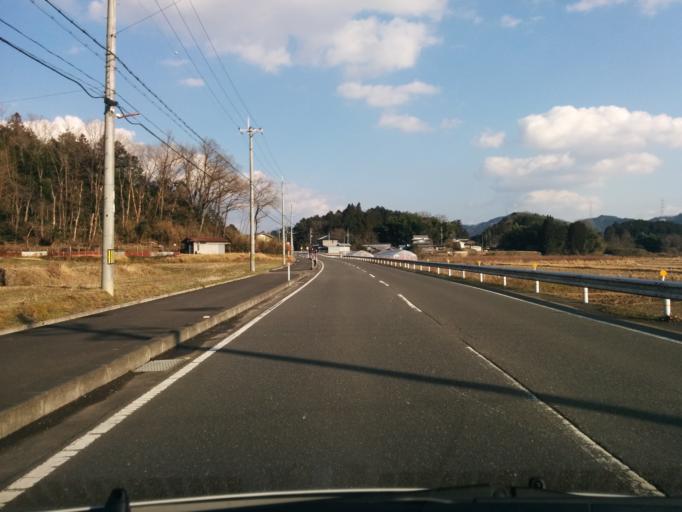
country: JP
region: Kyoto
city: Ayabe
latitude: 35.3613
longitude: 135.2124
